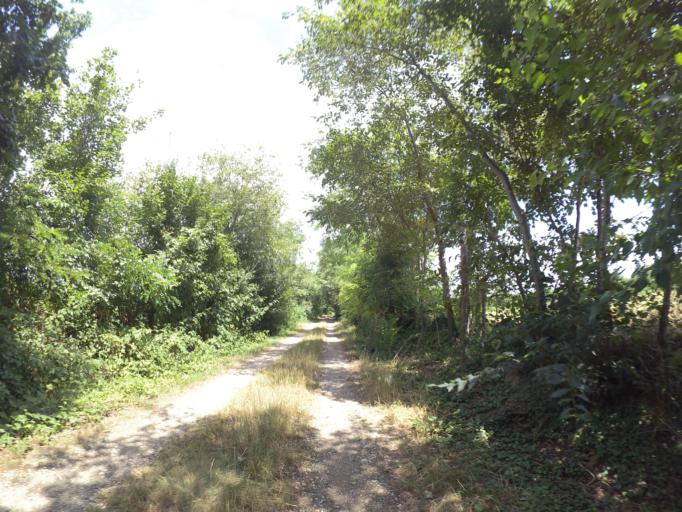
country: IT
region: Friuli Venezia Giulia
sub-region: Provincia di Udine
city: Bertiolo
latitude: 45.9640
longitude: 13.0595
